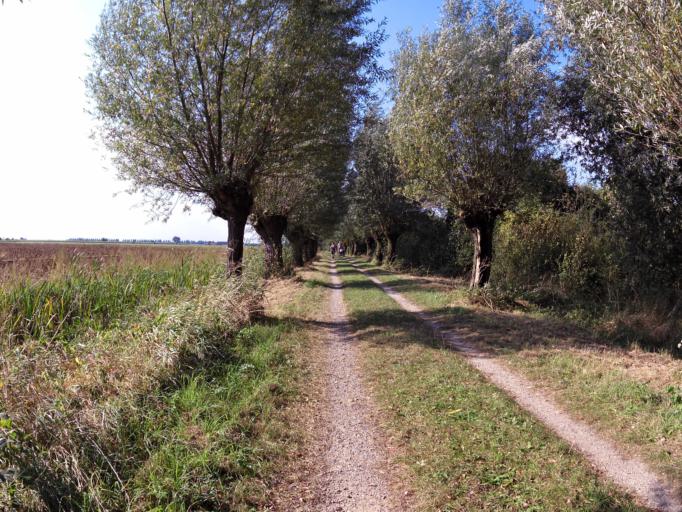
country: NL
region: North Brabant
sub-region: Gemeente Oss
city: Oss
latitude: 51.7914
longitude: 5.5228
